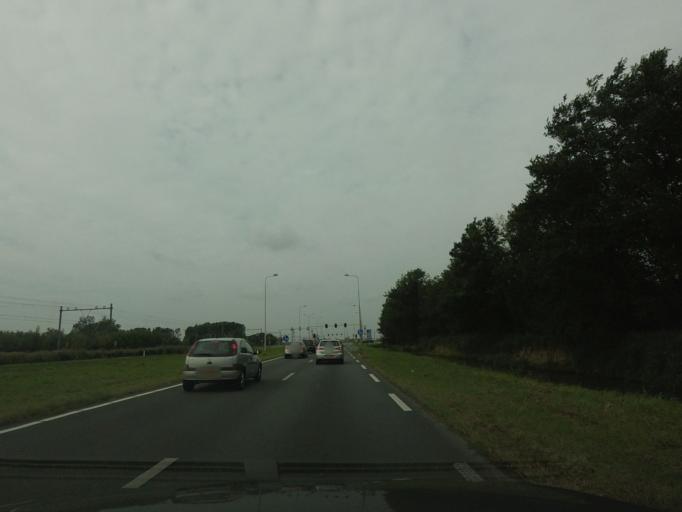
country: NL
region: North Holland
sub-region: Gemeente Uitgeest
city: Uitgeest
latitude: 52.5007
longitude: 4.7429
